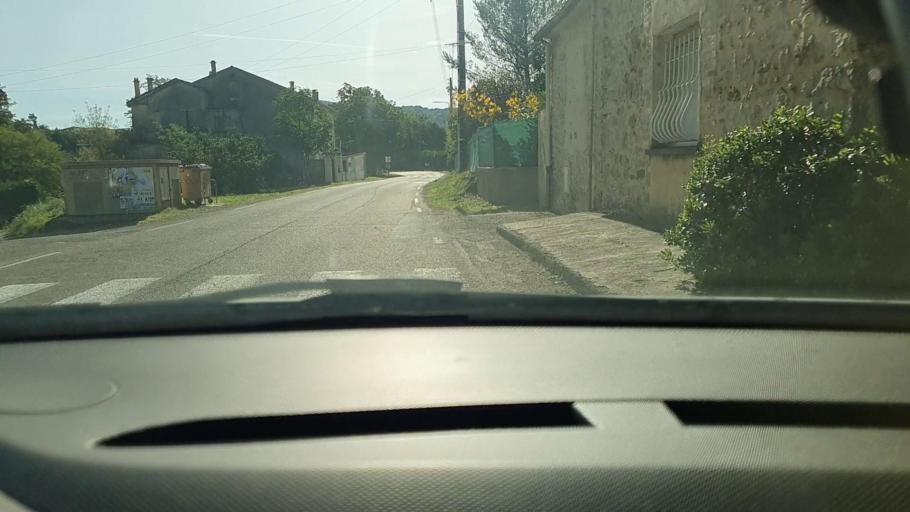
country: FR
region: Languedoc-Roussillon
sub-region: Departement du Gard
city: Saint-Florent-sur-Auzonnet
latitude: 44.2441
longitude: 4.1013
